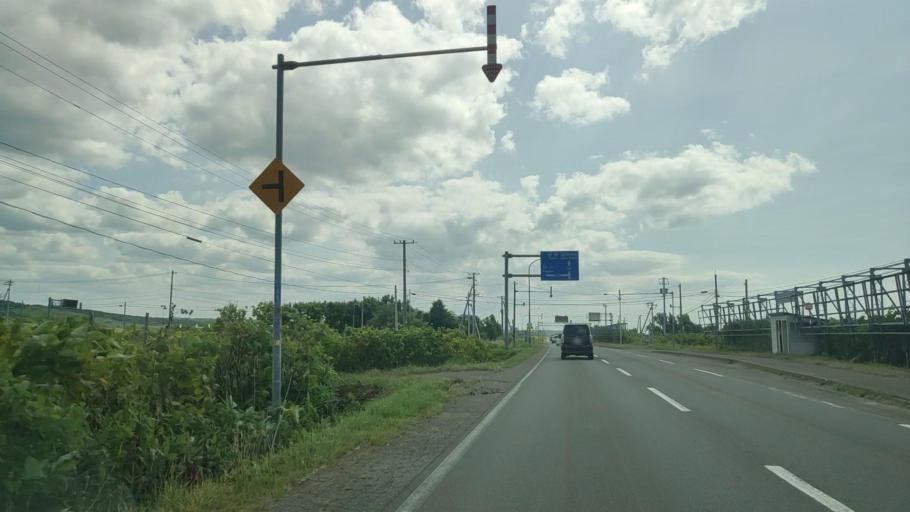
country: JP
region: Hokkaido
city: Makubetsu
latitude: 44.7565
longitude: 141.7946
